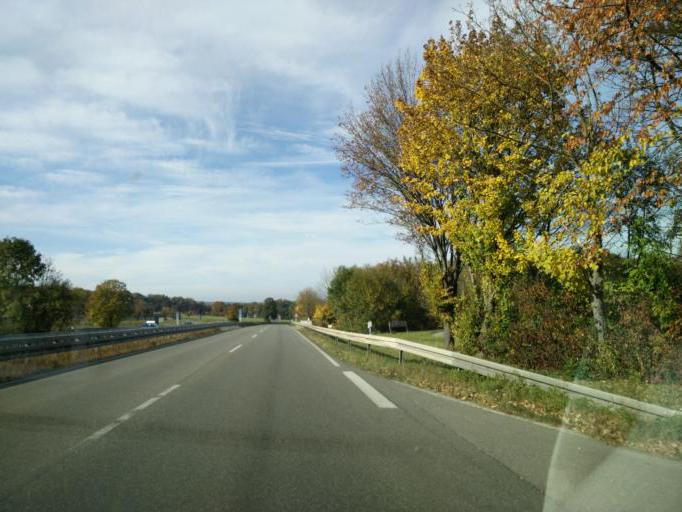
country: DE
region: Baden-Wuerttemberg
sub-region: Tuebingen Region
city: Kusterdingen
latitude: 48.5075
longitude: 9.1032
